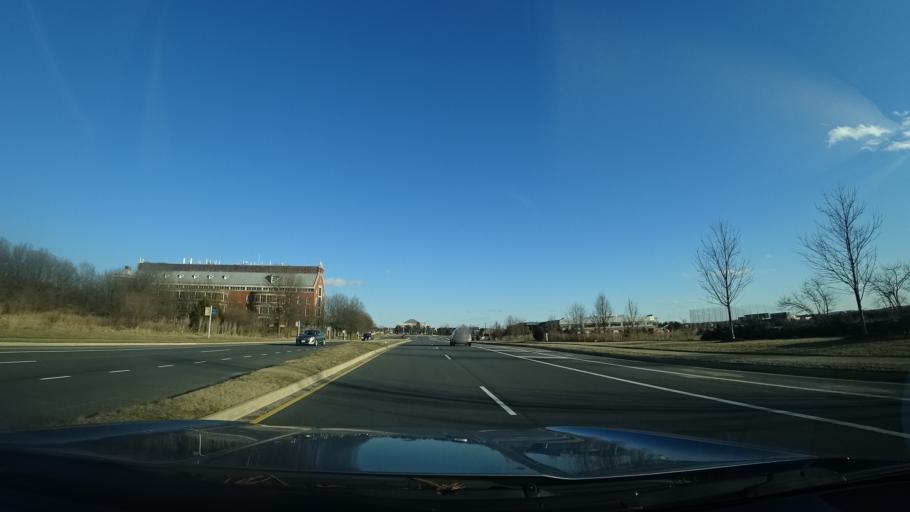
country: US
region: Virginia
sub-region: Loudoun County
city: University Center
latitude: 39.0601
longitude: -77.4484
